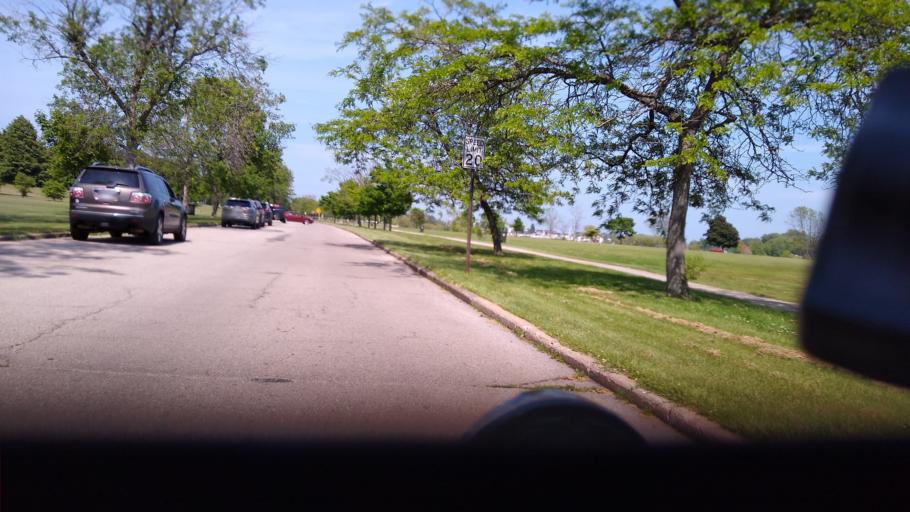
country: US
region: Michigan
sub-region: Delta County
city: Escanaba
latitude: 45.7403
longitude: -87.0520
